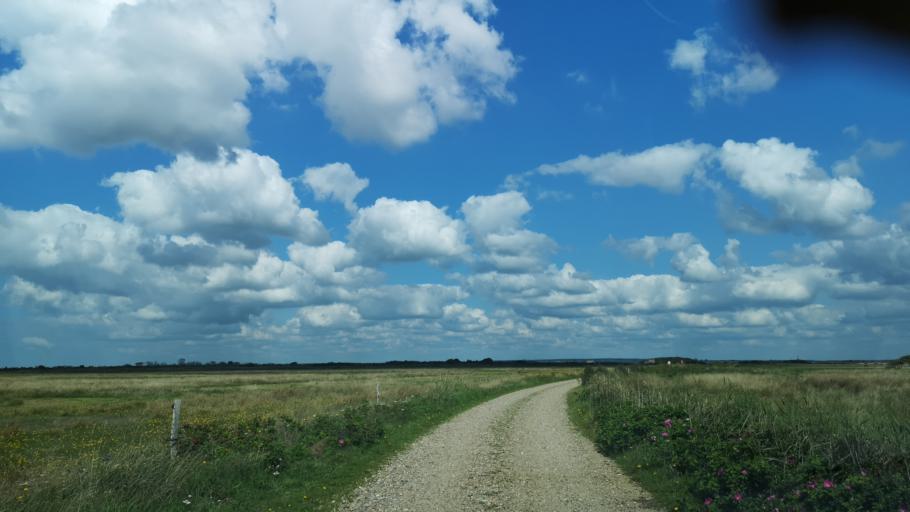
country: DK
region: Central Jutland
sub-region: Ringkobing-Skjern Kommune
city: Skjern
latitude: 55.9085
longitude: 8.4000
